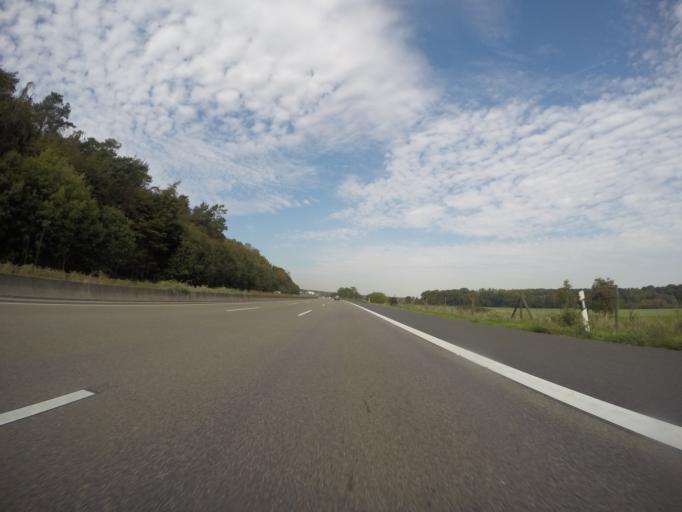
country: DE
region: Hesse
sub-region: Regierungsbezirk Darmstadt
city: Seligenstadt
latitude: 50.0423
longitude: 8.9331
